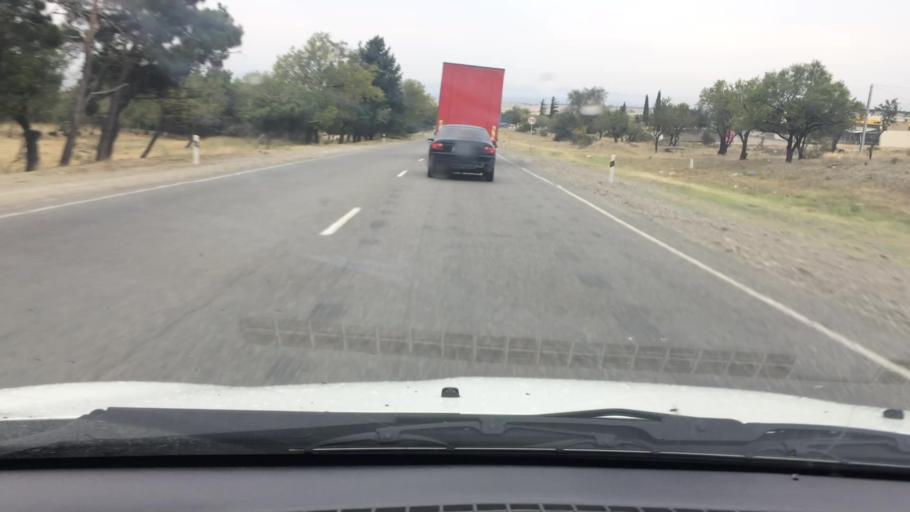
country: GE
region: T'bilisi
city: Tbilisi
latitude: 41.6405
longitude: 44.8652
